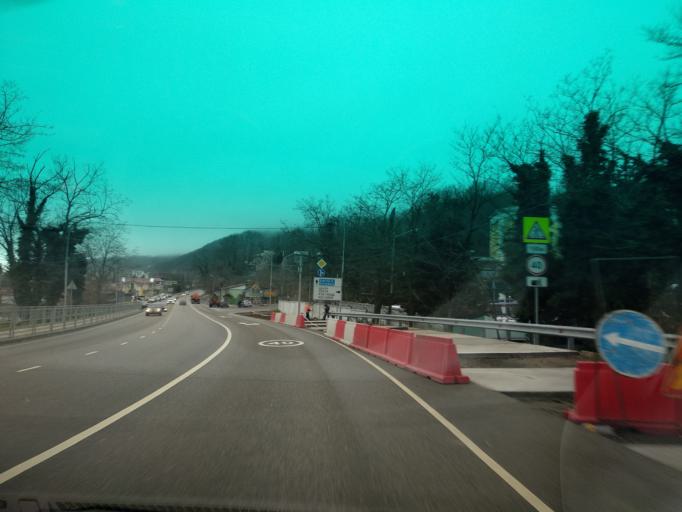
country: RU
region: Krasnodarskiy
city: Tuapse
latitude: 44.1161
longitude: 39.0659
